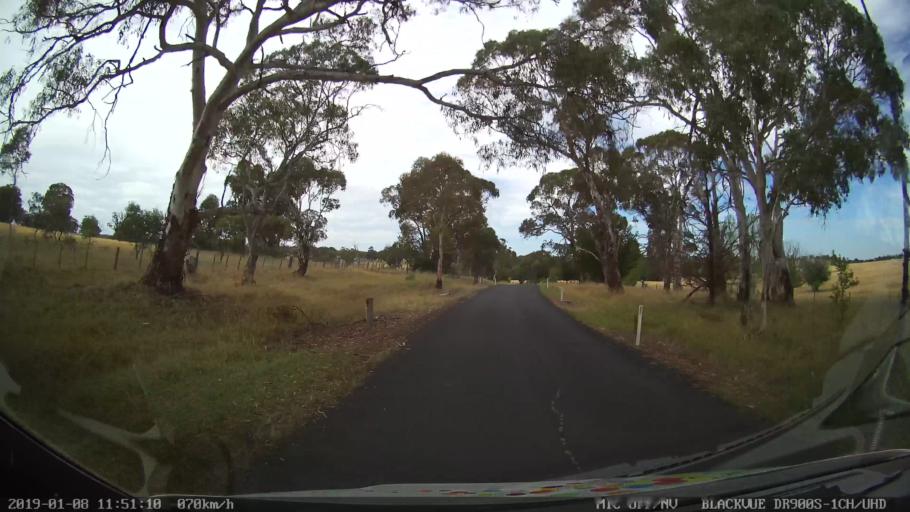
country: AU
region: New South Wales
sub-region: Armidale Dumaresq
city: Armidale
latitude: -30.3902
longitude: 151.5589
